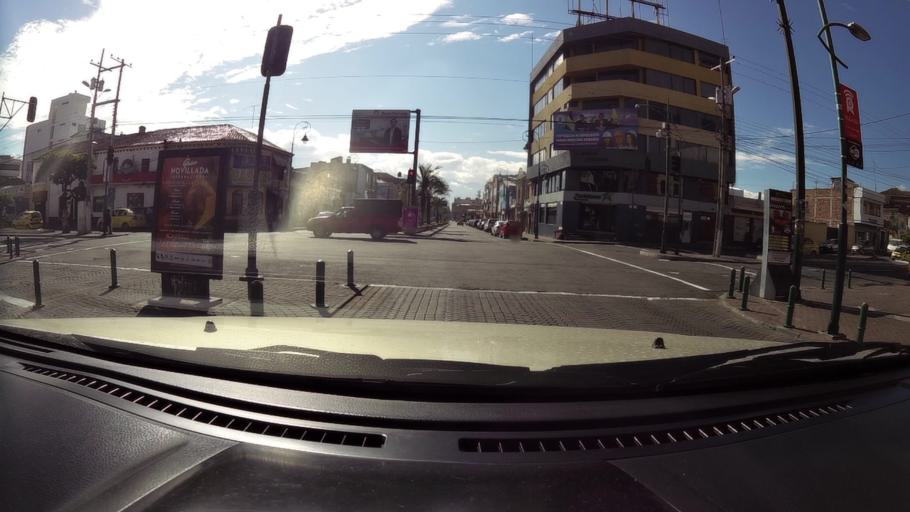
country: EC
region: Chimborazo
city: Riobamba
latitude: -1.6680
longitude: -78.6555
